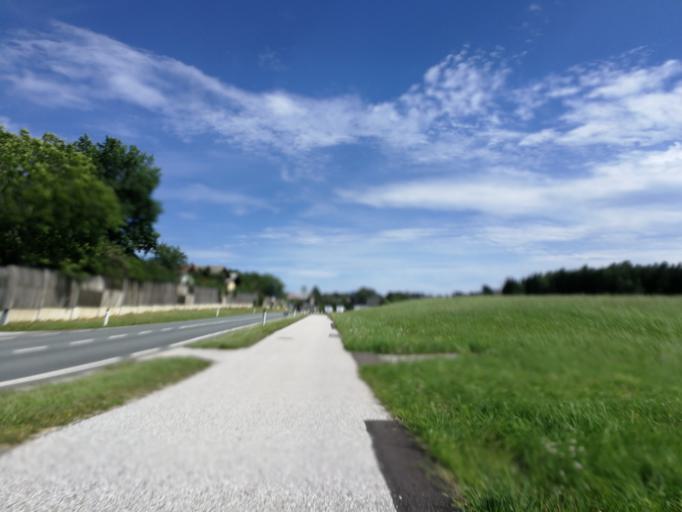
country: AT
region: Salzburg
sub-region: Politischer Bezirk Salzburg-Umgebung
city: Eugendorf
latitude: 47.8624
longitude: 13.1397
